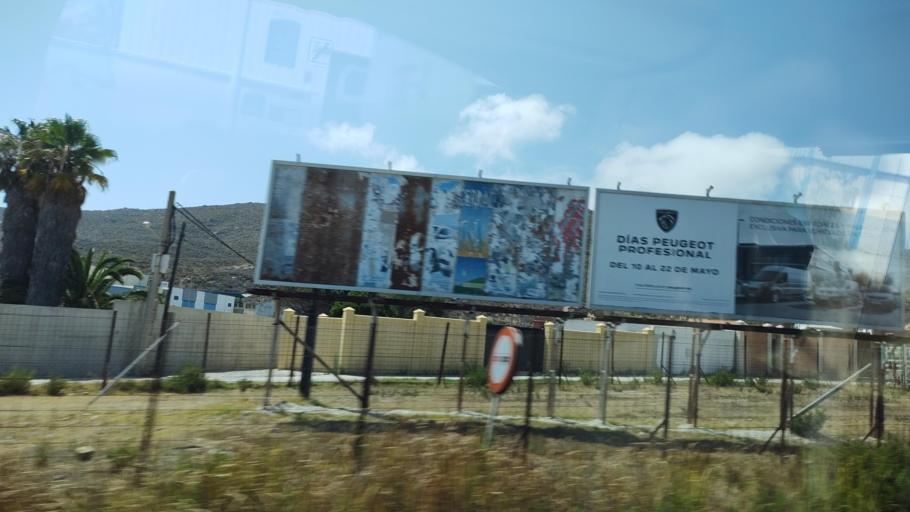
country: ES
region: Andalusia
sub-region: Provincia de Cadiz
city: La Linea de la Concepcion
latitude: 36.1918
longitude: -5.3486
